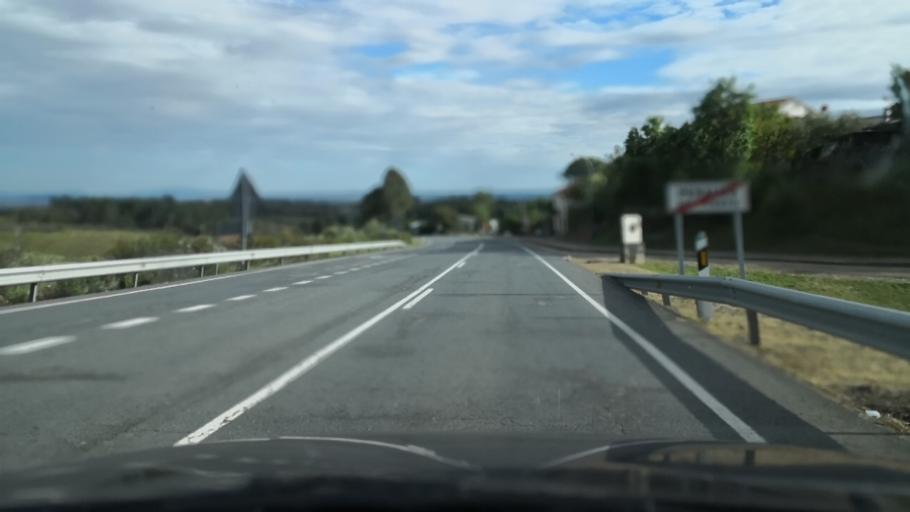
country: ES
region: Extremadura
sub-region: Provincia de Caceres
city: Perales del Puerto
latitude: 40.1536
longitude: -6.6793
